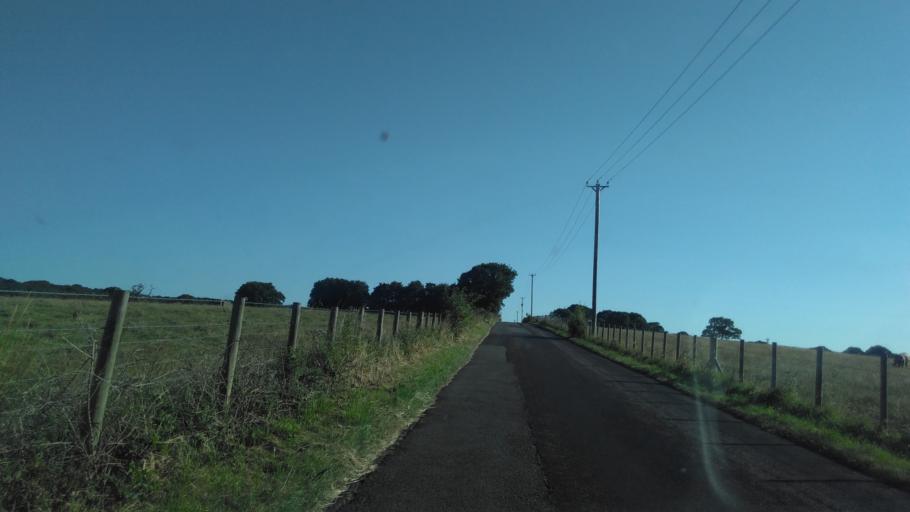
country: GB
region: England
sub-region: Kent
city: Dunkirk
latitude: 51.3022
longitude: 0.9861
